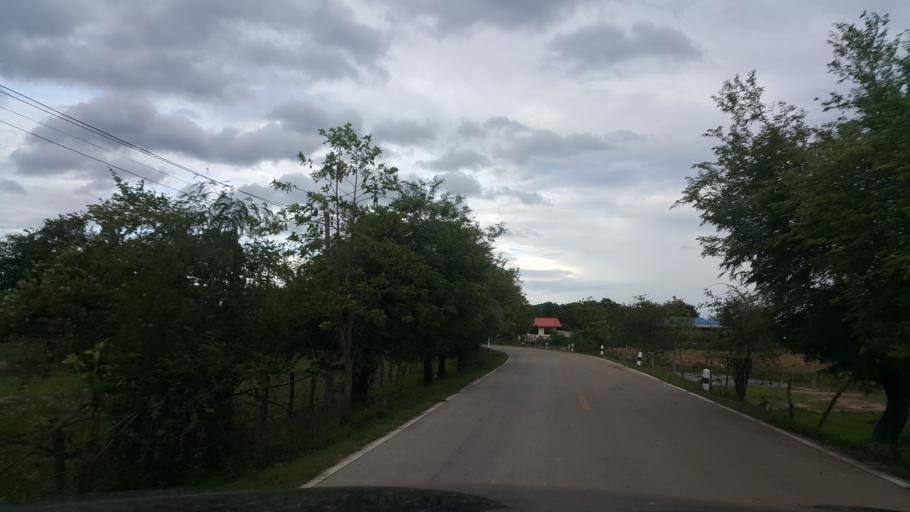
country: TH
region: Sukhothai
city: Ban Dan Lan Hoi
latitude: 17.1553
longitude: 99.5143
